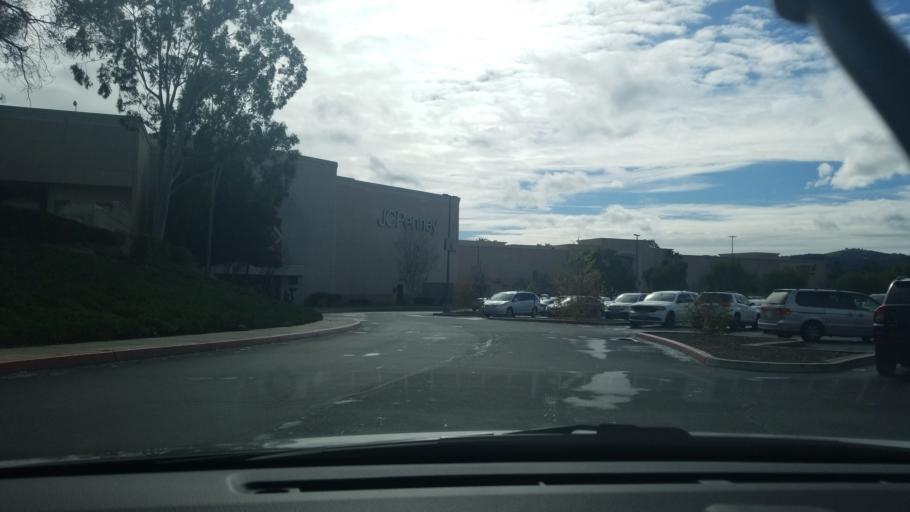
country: US
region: California
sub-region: Riverside County
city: Temecula
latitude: 33.5264
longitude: -117.1551
